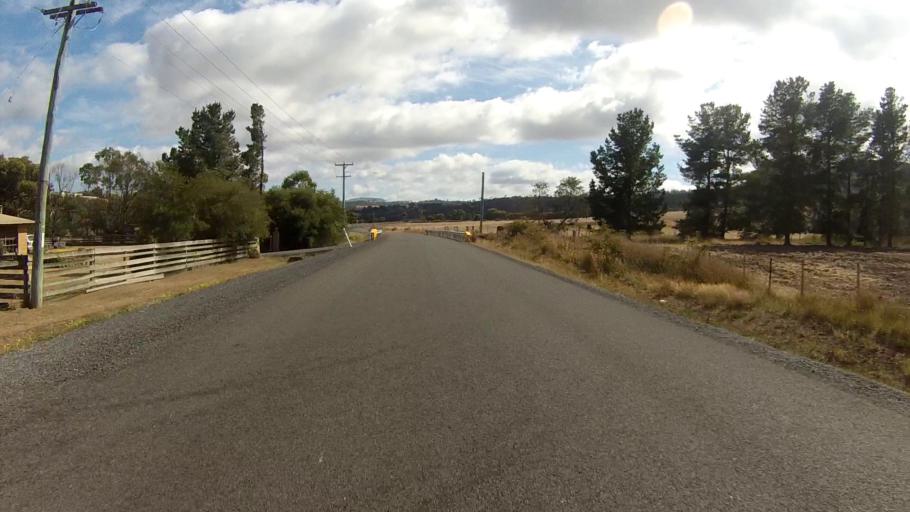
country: AU
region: Tasmania
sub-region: Brighton
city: Old Beach
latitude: -42.7634
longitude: 147.3004
